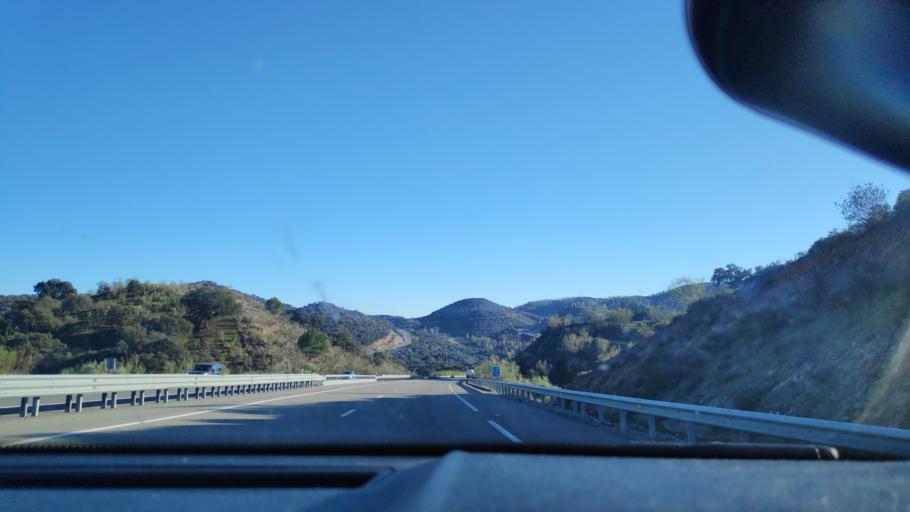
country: ES
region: Andalusia
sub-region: Provincia de Sevilla
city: El Ronquillo
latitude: 37.6765
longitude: -6.1759
